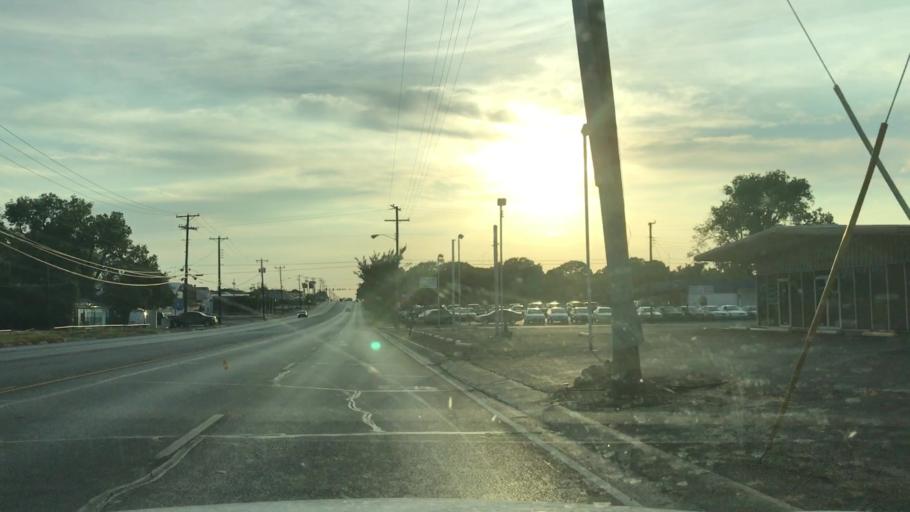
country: US
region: Texas
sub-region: Tarrant County
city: Haltom City
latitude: 32.7951
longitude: -97.2859
